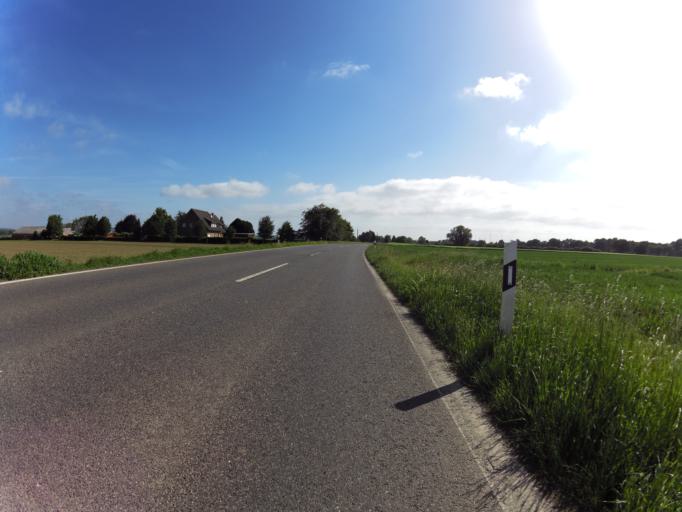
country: DE
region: North Rhine-Westphalia
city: Huckelhoven
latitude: 51.0065
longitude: 6.2223
